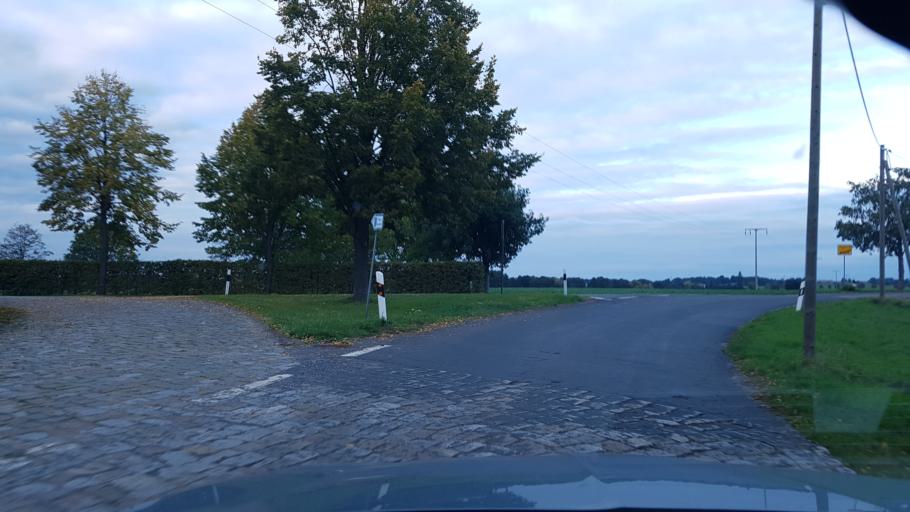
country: DE
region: Saxony
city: Priestewitz
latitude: 51.2419
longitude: 13.5642
